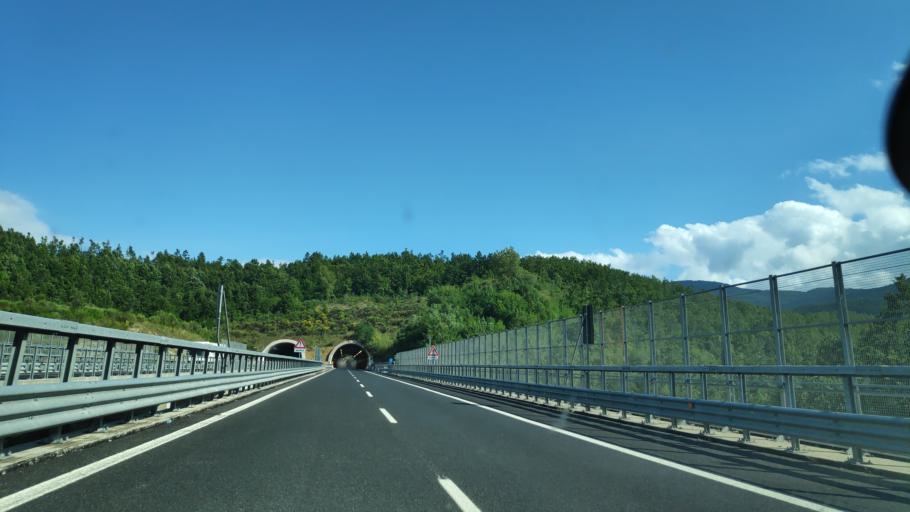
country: IT
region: Campania
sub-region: Provincia di Salerno
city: Casalbuono
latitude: 40.2350
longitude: 15.6629
